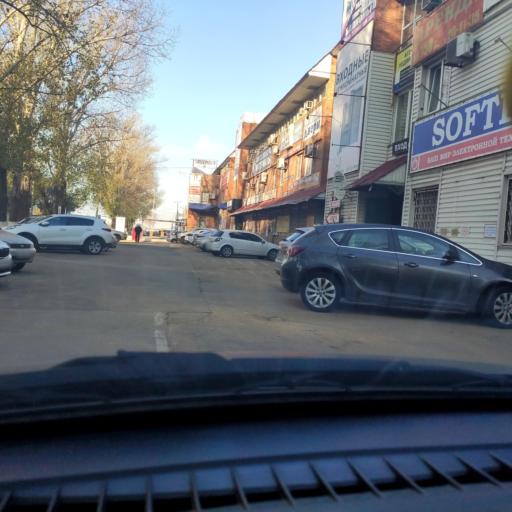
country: RU
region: Samara
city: Tol'yatti
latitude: 53.5392
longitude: 49.2668
